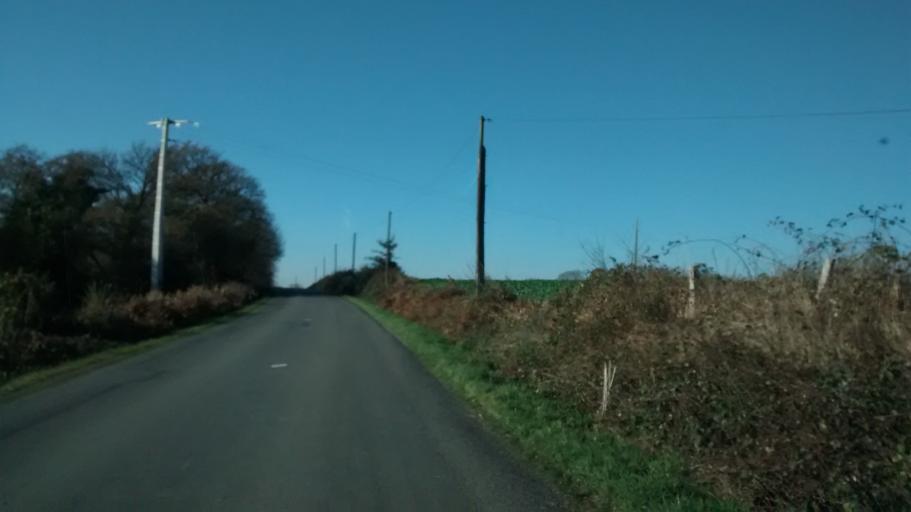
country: FR
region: Brittany
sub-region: Departement d'Ille-et-Vilaine
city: La Bouexiere
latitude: 48.1978
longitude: -1.4509
